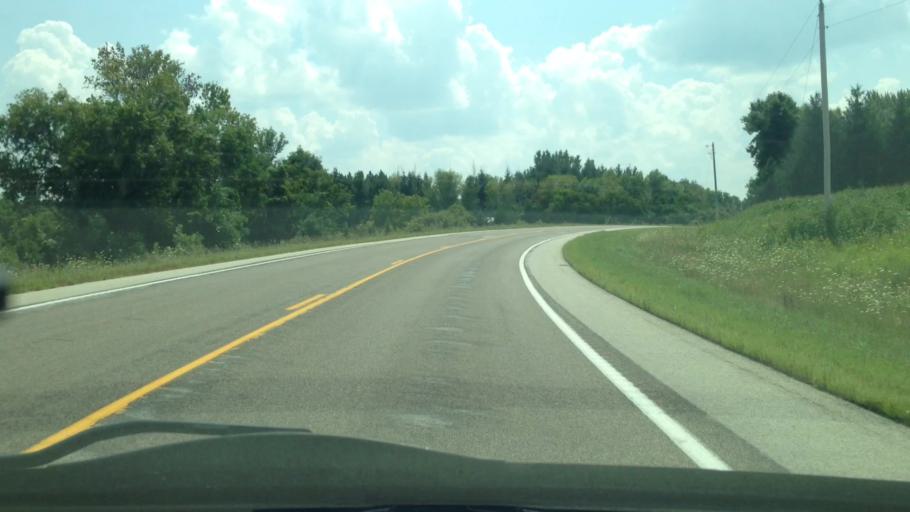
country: US
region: Minnesota
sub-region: Olmsted County
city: Stewartville
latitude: 43.9005
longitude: -92.4086
